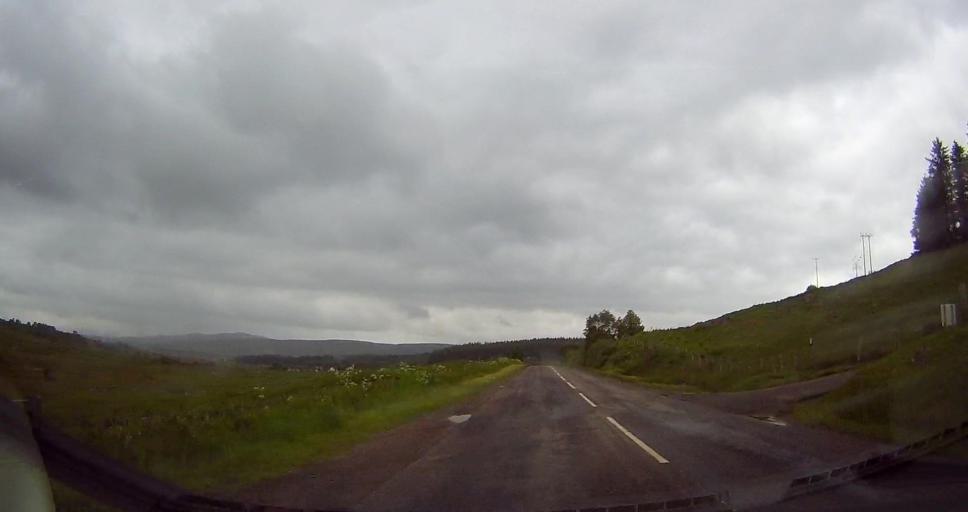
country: GB
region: Scotland
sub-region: Highland
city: Alness
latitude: 58.0181
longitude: -4.3605
